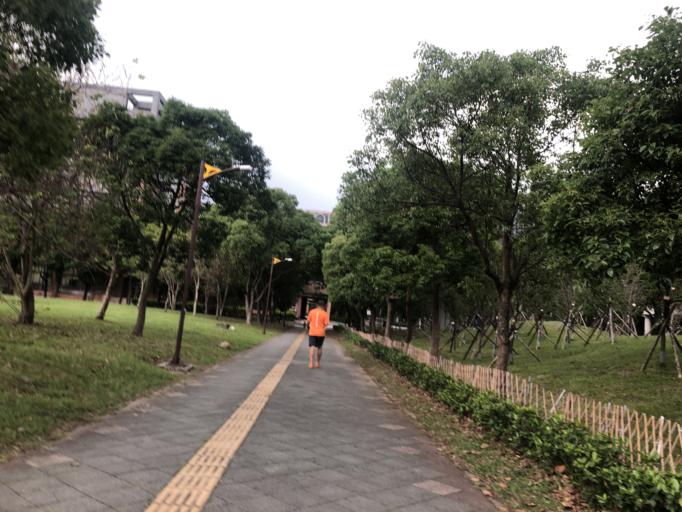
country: TW
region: Taiwan
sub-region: Taoyuan
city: Taoyuan
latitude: 24.9433
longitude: 121.3688
